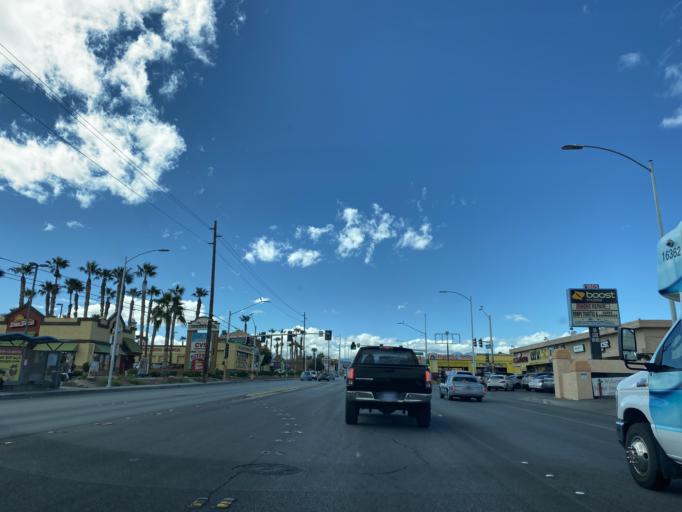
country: US
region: Nevada
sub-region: Clark County
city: Las Vegas
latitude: 36.1589
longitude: -115.1240
